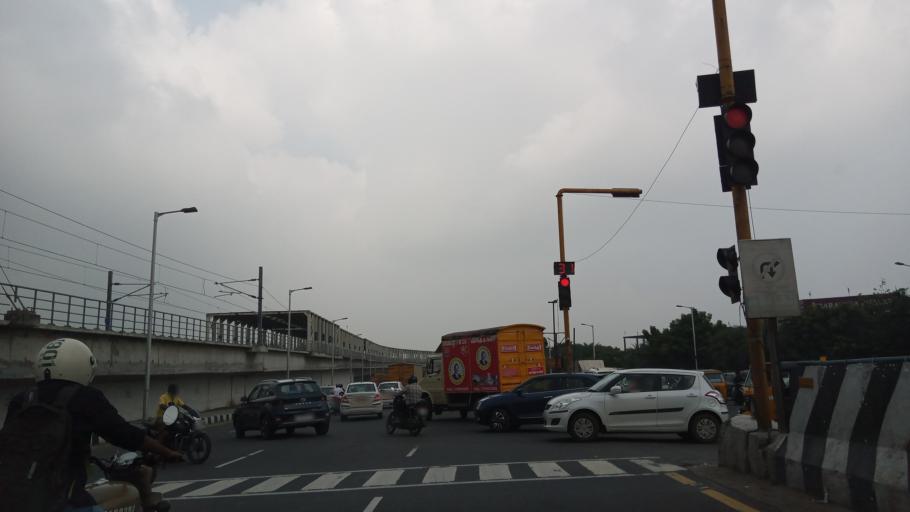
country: IN
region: Tamil Nadu
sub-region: Kancheepuram
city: Saint Thomas Mount
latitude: 12.9960
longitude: 80.1891
